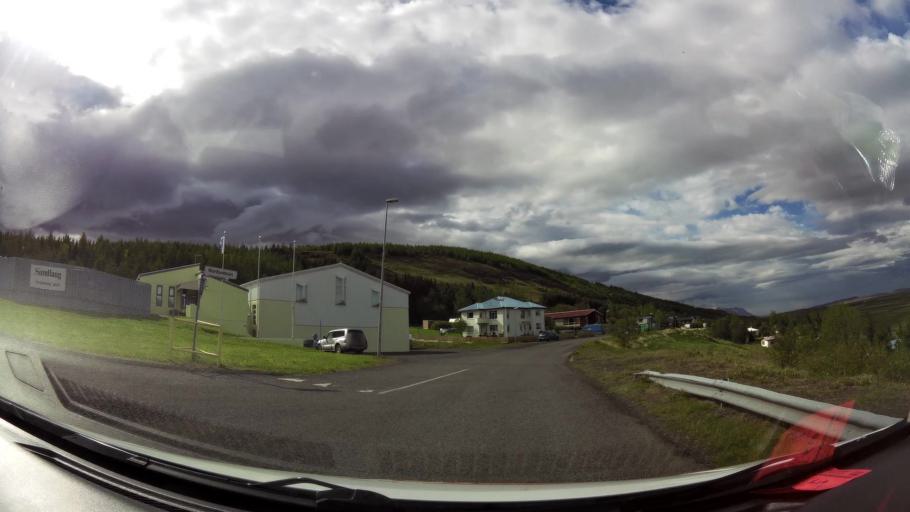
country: IS
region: Northwest
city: Saudarkrokur
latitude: 65.5534
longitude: -19.4498
